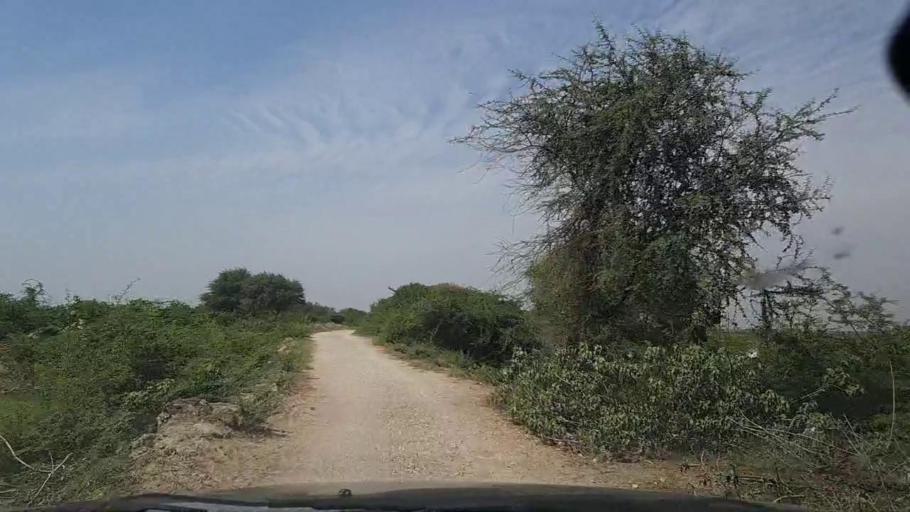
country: PK
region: Sindh
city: Mirpur Batoro
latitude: 24.6528
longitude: 68.1673
